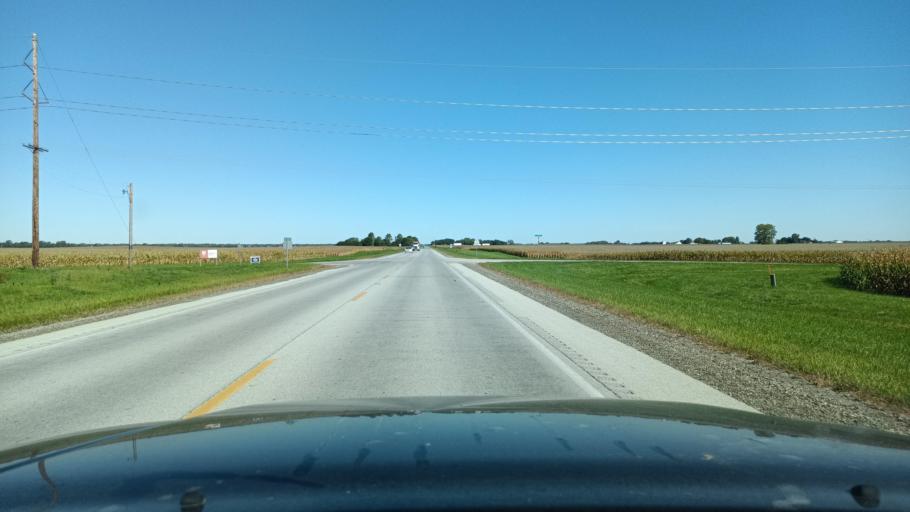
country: US
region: Illinois
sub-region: Champaign County
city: Philo
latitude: 40.0540
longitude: -88.1618
